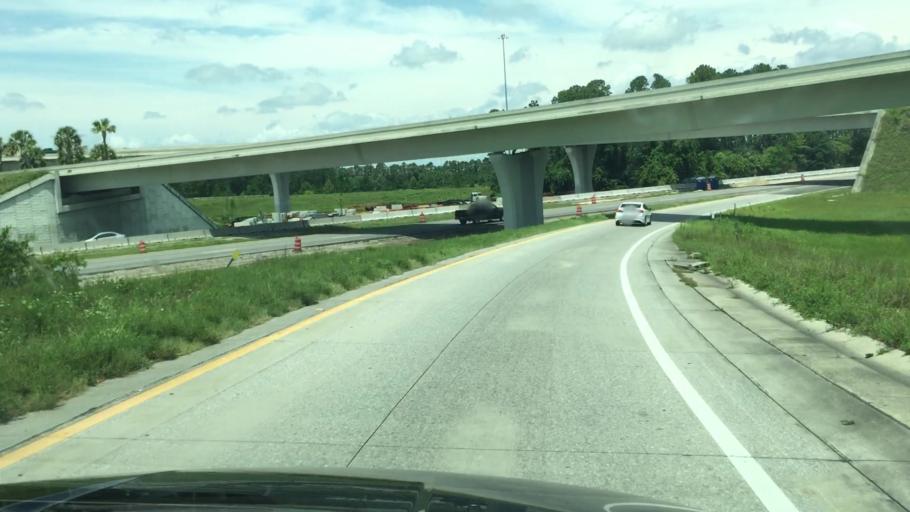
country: US
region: Florida
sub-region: Duval County
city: Jacksonville Beach
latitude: 30.2547
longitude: -81.5160
